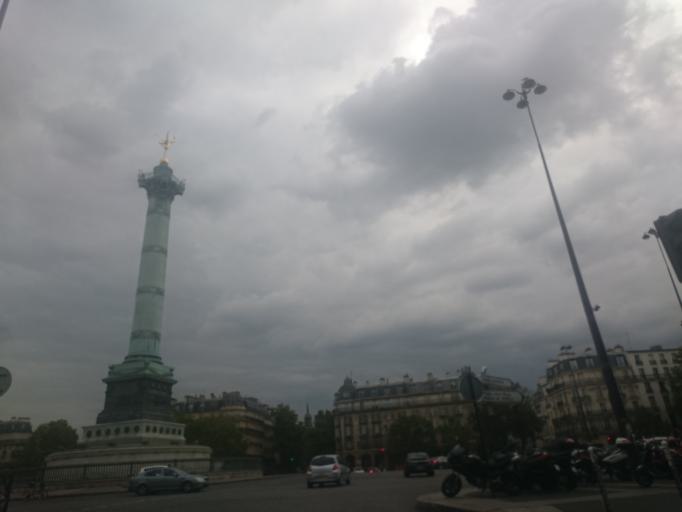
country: FR
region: Ile-de-France
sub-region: Paris
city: Paris
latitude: 48.8534
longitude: 2.3700
